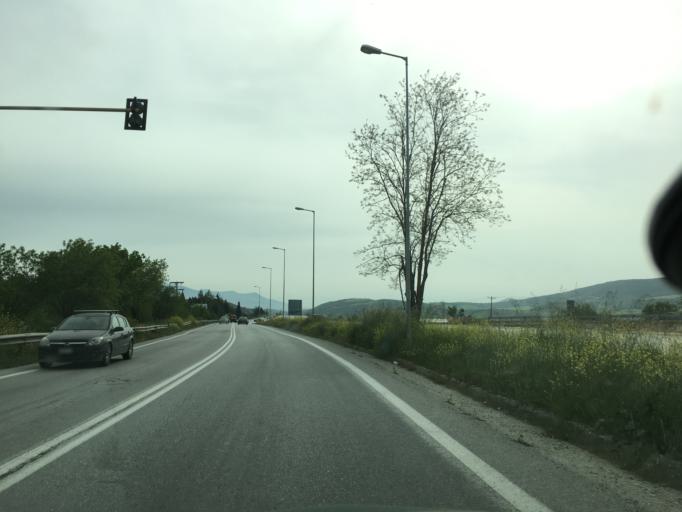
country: GR
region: Thessaly
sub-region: Nomos Magnisias
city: Velestino
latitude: 39.3873
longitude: 22.7810
